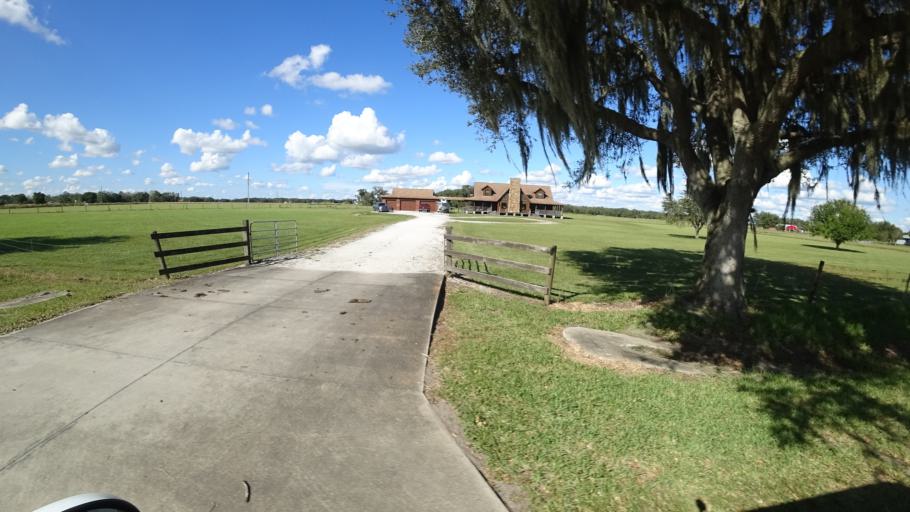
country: US
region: Florida
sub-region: Sarasota County
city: Warm Mineral Springs
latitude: 27.2740
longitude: -82.2069
